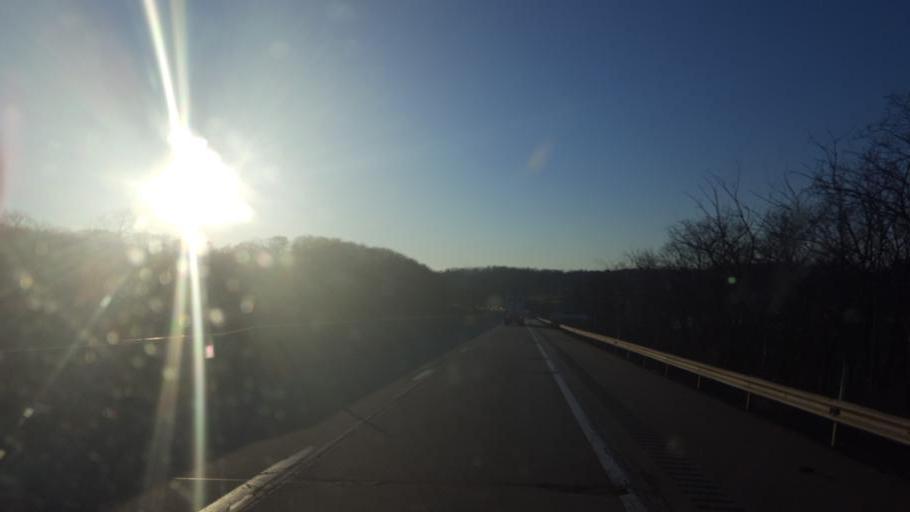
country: US
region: Pennsylvania
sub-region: Washington County
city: East Washington
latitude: 40.1659
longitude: -80.1681
